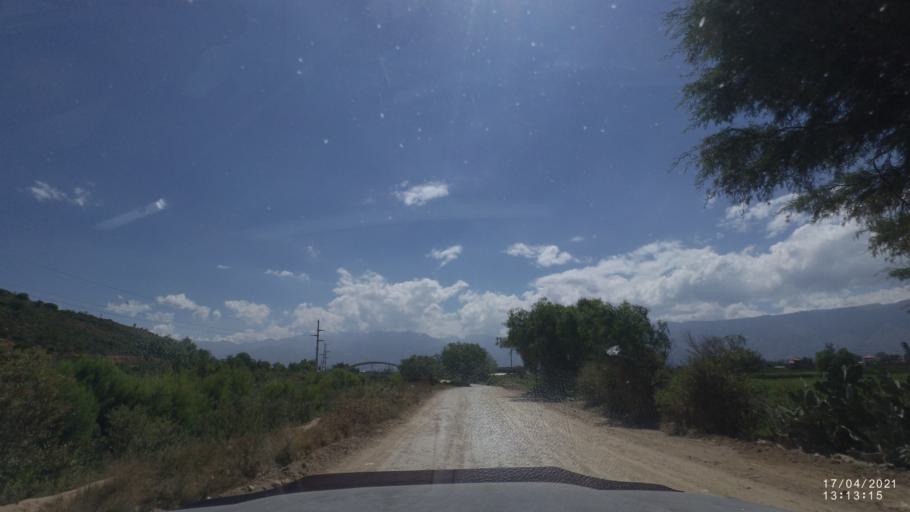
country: BO
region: Cochabamba
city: Cochabamba
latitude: -17.4194
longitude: -66.2229
